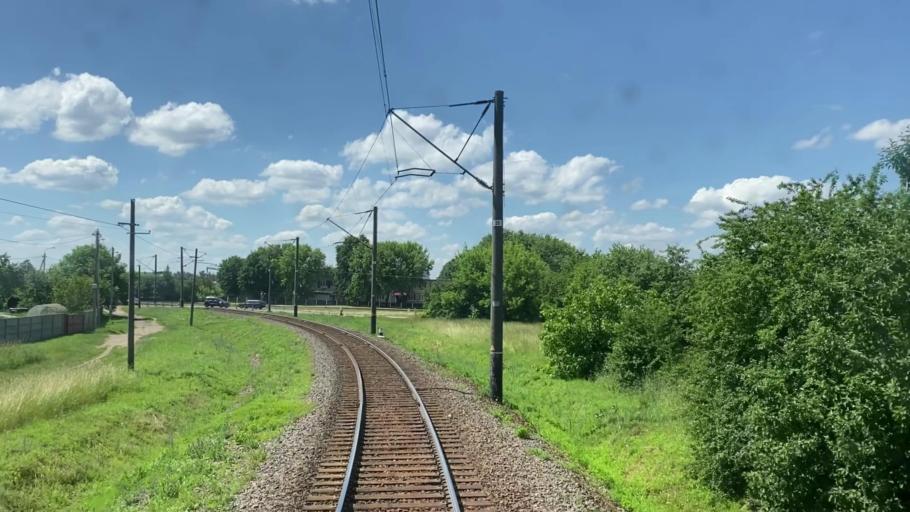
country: BY
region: Brest
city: Baranovichi
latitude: 53.1412
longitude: 26.0323
